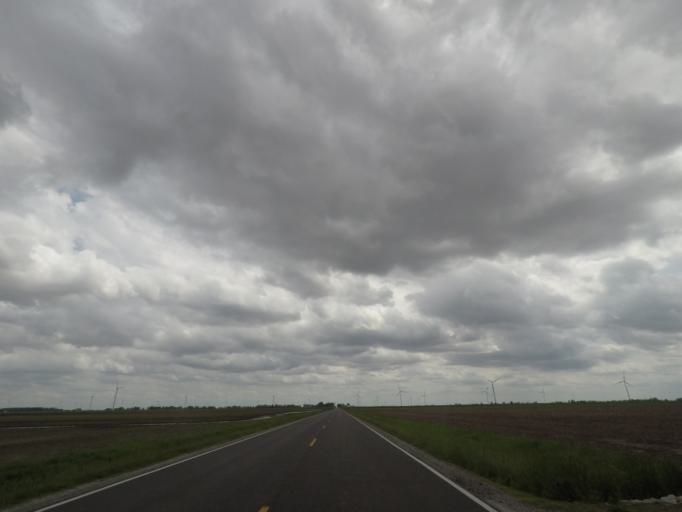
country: US
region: Illinois
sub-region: Macon County
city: Warrensburg
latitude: 40.0405
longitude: -89.0856
